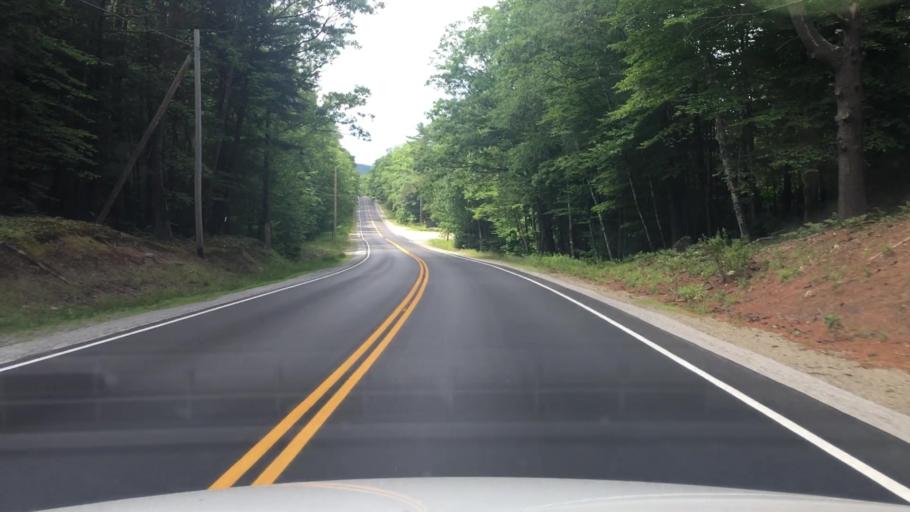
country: US
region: Maine
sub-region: Oxford County
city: West Paris
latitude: 44.3947
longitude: -70.6639
